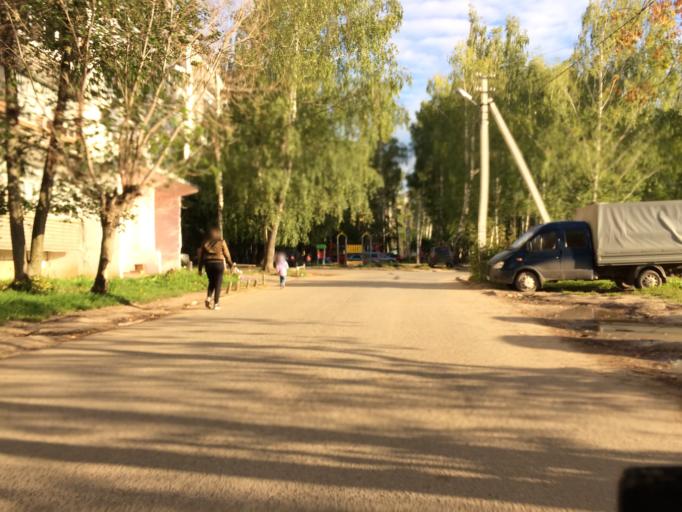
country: RU
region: Mariy-El
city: Yoshkar-Ola
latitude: 56.6508
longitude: 47.9713
